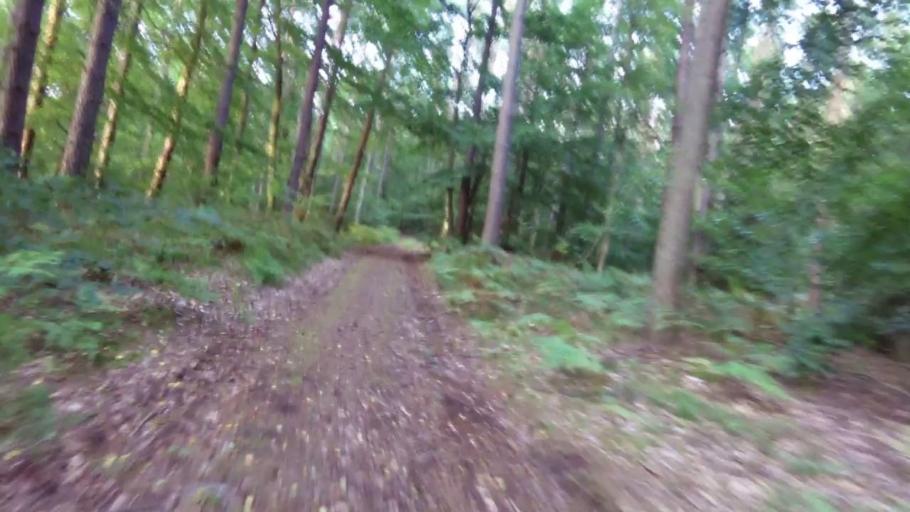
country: PL
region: West Pomeranian Voivodeship
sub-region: Powiat drawski
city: Zlocieniec
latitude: 53.5604
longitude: 16.0166
